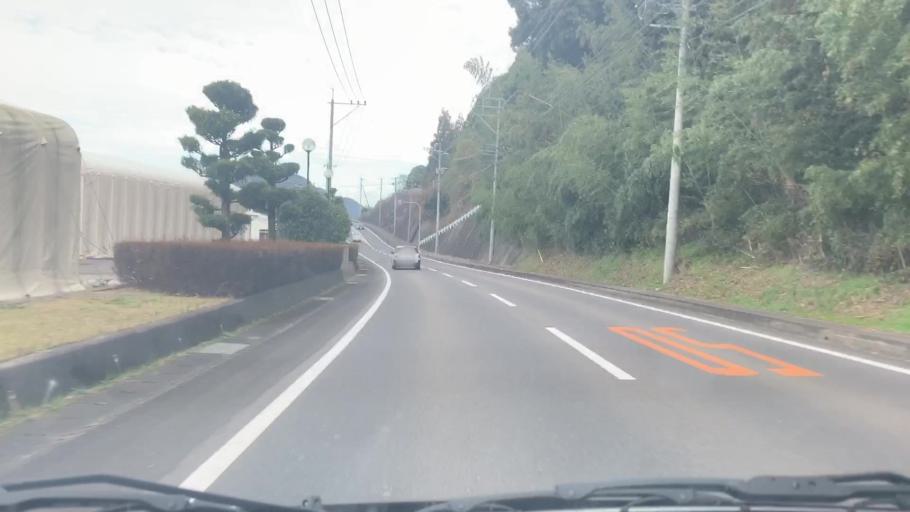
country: JP
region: Saga Prefecture
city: Imaricho-ko
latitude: 33.2887
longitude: 129.9709
